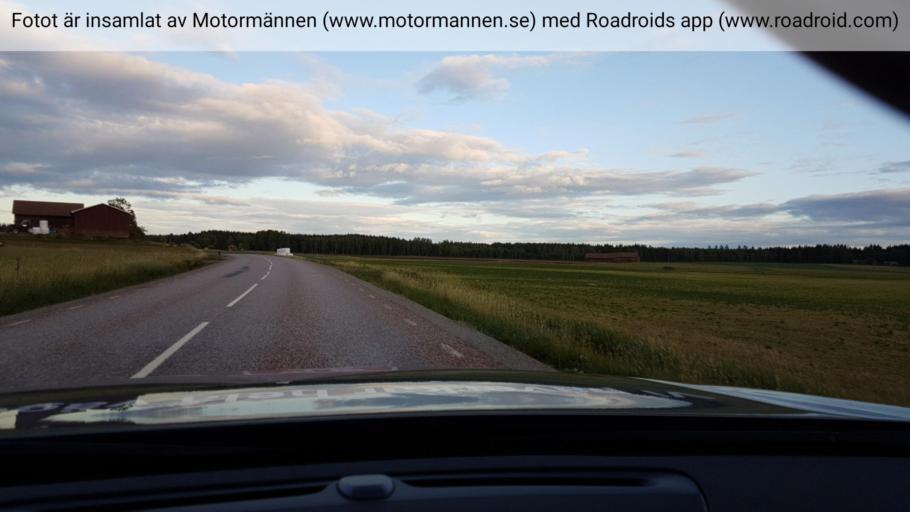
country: SE
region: Vaestmanland
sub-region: Vasteras
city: Skultuna
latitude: 59.8802
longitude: 16.3772
